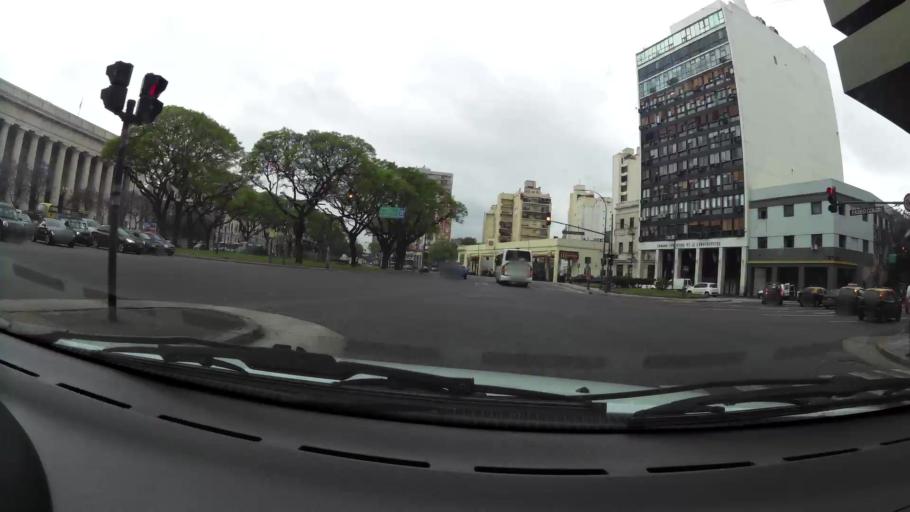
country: AR
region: Buenos Aires F.D.
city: Buenos Aires
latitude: -34.6170
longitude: -58.3693
